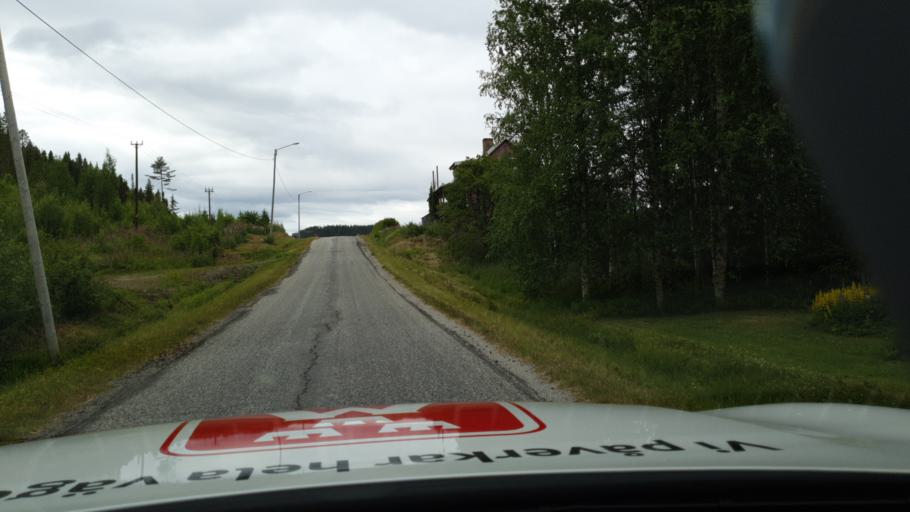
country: SE
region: Vaesterbotten
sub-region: Dorotea Kommun
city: Dorotea
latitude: 64.1243
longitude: 16.3084
